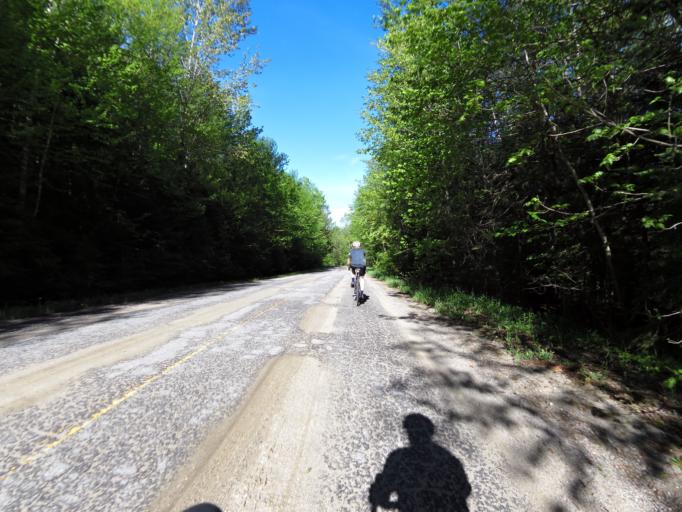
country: CA
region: Quebec
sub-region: Outaouais
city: Wakefield
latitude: 45.6115
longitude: -75.8628
